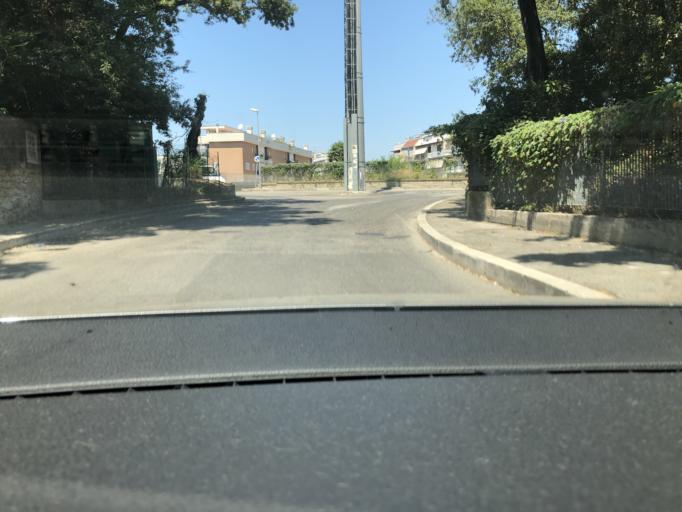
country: IT
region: Latium
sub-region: Citta metropolitana di Roma Capitale
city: Anzio
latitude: 41.4585
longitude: 12.6439
